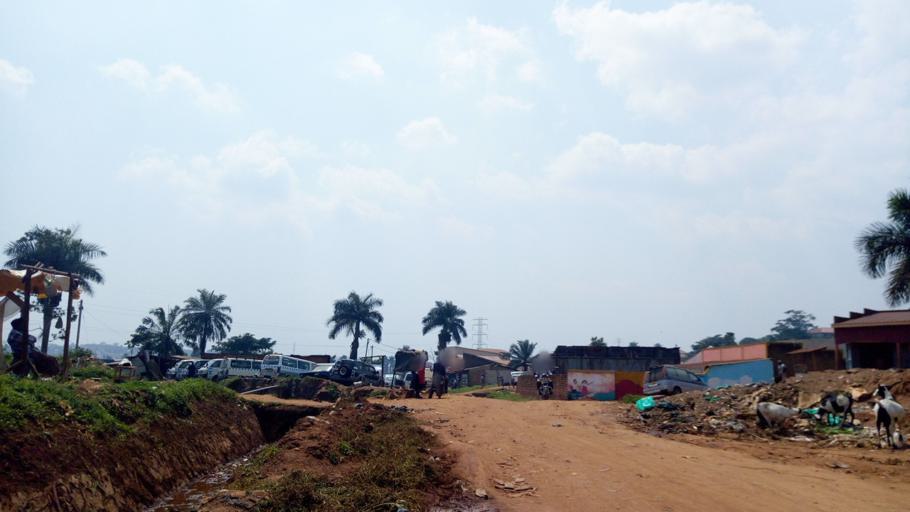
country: UG
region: Central Region
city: Kampala Central Division
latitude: 0.3451
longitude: 32.5567
